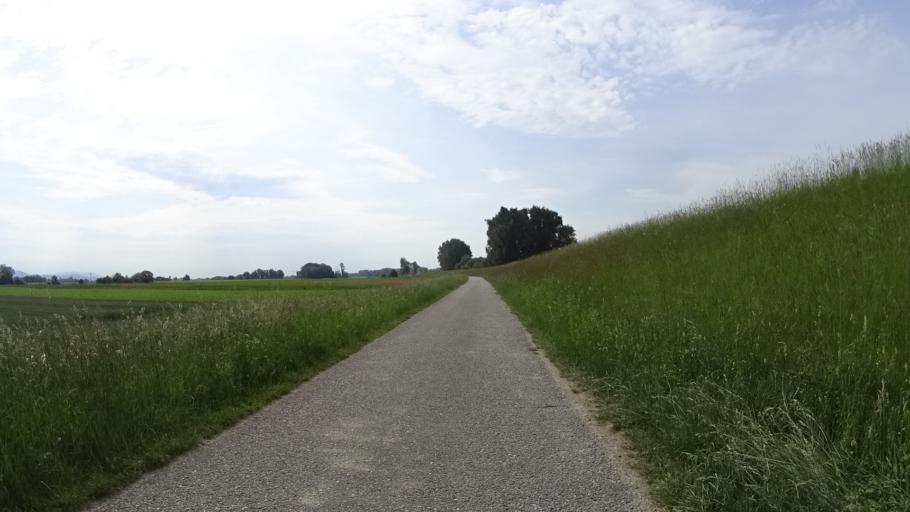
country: DE
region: Bavaria
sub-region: Lower Bavaria
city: Irlbach
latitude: 48.8408
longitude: 12.7707
